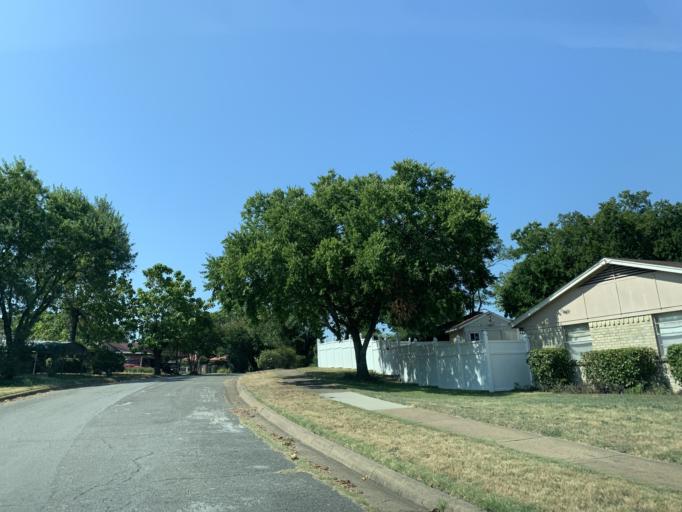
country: US
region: Texas
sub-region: Dallas County
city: Hutchins
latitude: 32.6624
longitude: -96.7553
